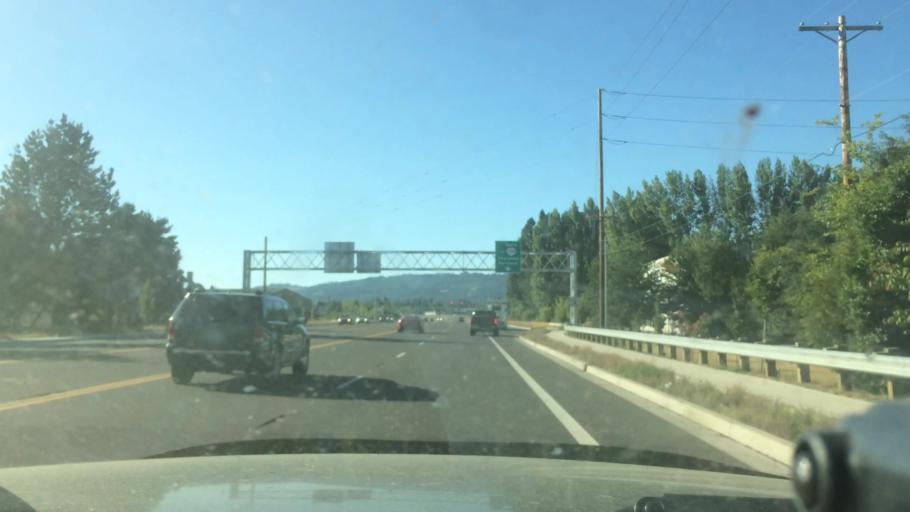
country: US
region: Oregon
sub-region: Yamhill County
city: Newberg
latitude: 45.2913
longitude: -122.9481
